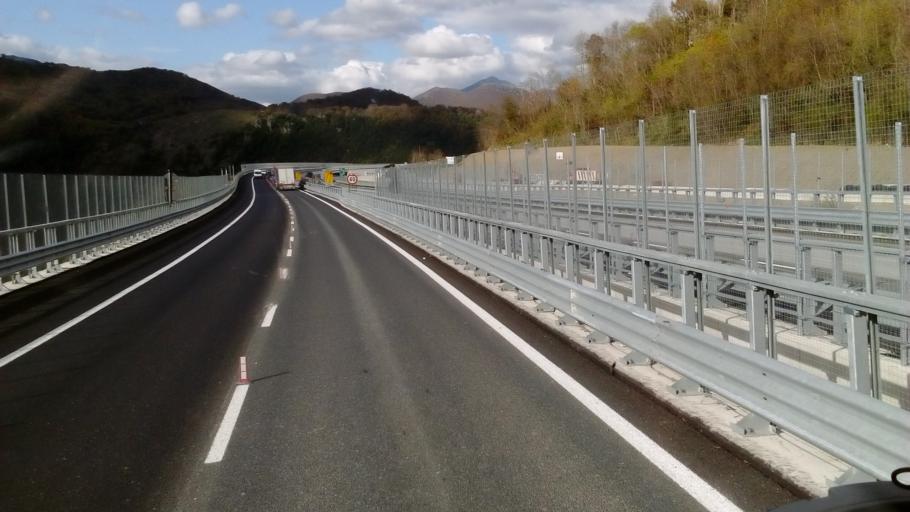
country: IT
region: Calabria
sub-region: Provincia di Cosenza
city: Laino Castello-Nuovo Centro
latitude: 39.9313
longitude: 15.9634
